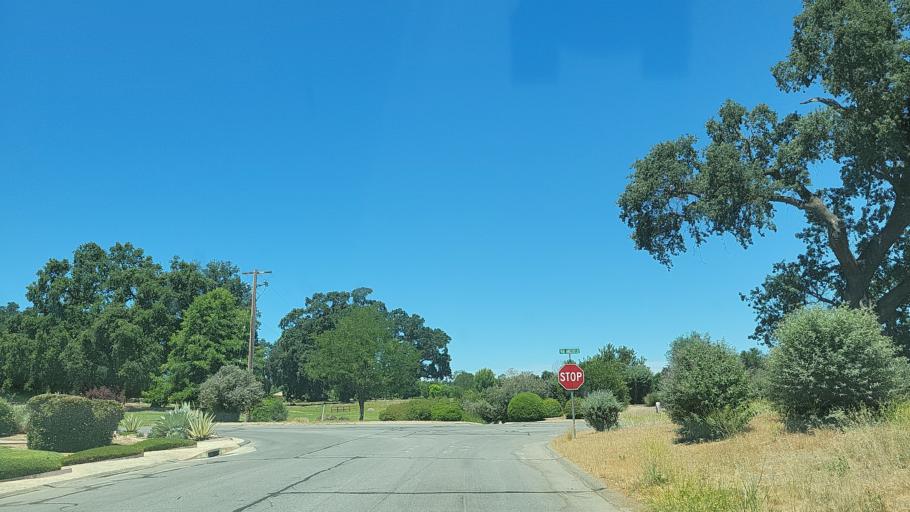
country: US
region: California
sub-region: San Luis Obispo County
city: Atascadero
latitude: 35.5122
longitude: -120.6699
